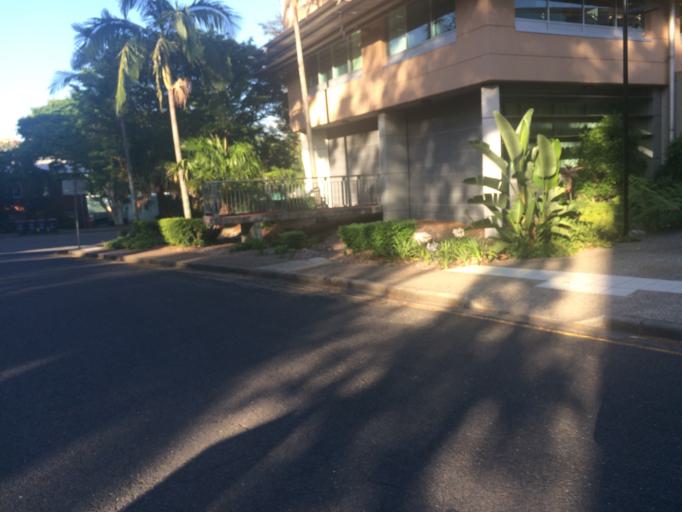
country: AU
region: Queensland
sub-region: Brisbane
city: South Brisbane
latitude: -27.4951
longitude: 153.0151
